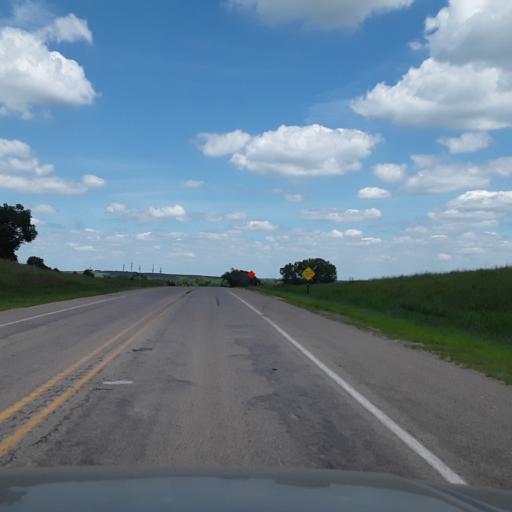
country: US
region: Nebraska
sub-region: Nance County
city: Genoa
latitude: 41.4730
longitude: -97.6997
